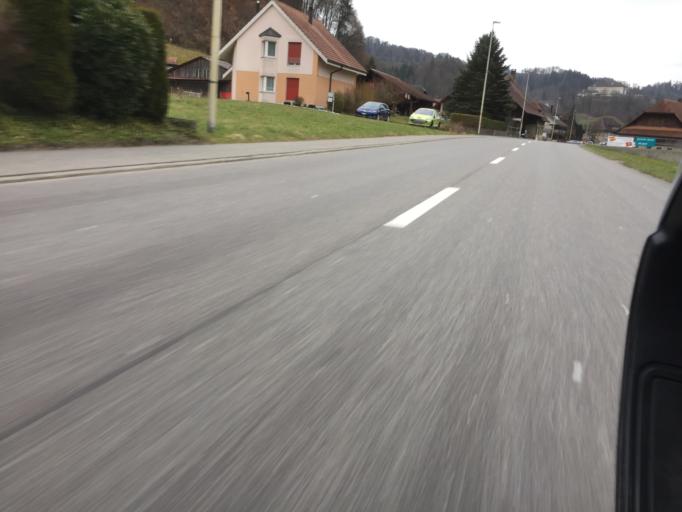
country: CH
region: Bern
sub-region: Emmental District
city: Krauchthal
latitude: 47.0126
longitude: 7.5677
